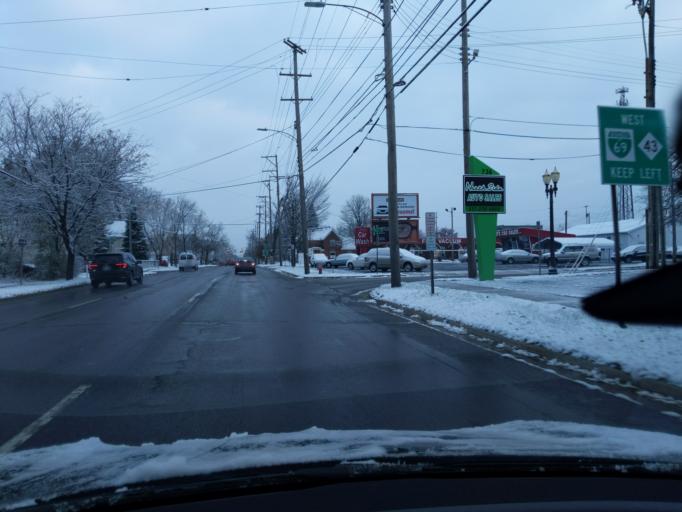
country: US
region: Michigan
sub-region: Ingham County
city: Lansing
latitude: 42.7419
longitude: -84.5446
